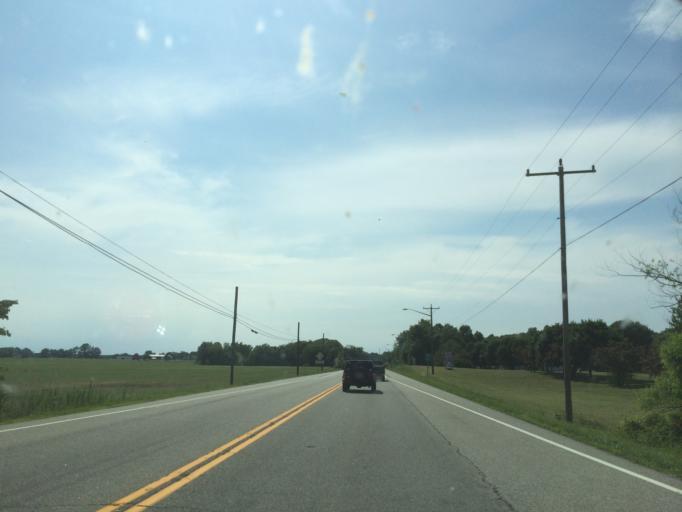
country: US
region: Maryland
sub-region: Queen Anne's County
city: Centreville
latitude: 38.9380
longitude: -76.0556
